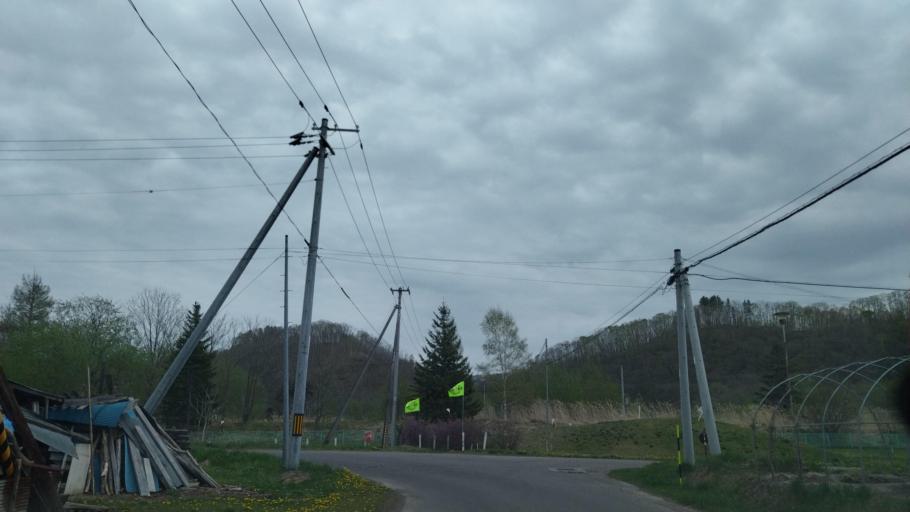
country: JP
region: Hokkaido
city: Kitami
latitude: 43.3540
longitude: 143.6057
